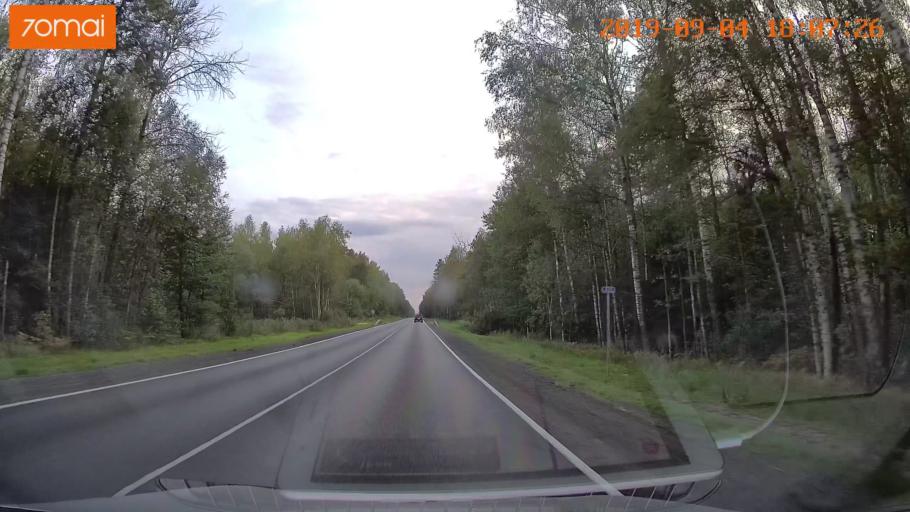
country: RU
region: Moskovskaya
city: Khorlovo
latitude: 55.4189
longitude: 38.8007
